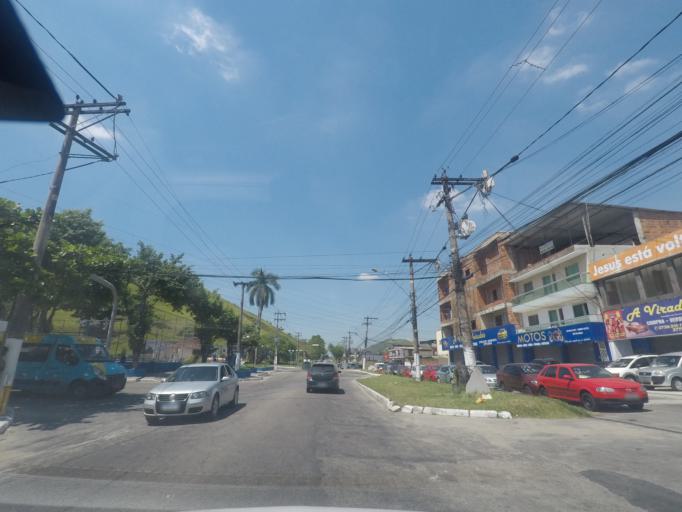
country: BR
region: Rio de Janeiro
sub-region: Petropolis
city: Petropolis
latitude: -22.6025
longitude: -43.1898
